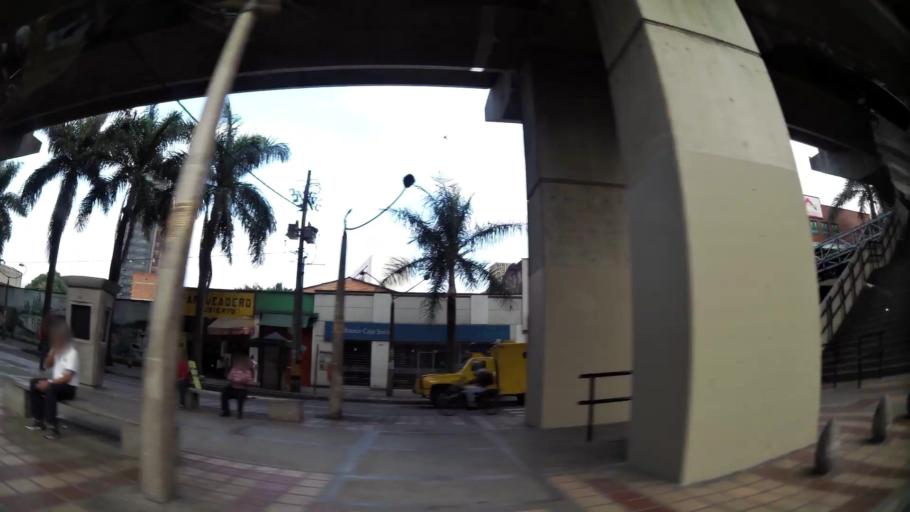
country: CO
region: Antioquia
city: Medellin
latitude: 6.2433
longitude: -75.5713
